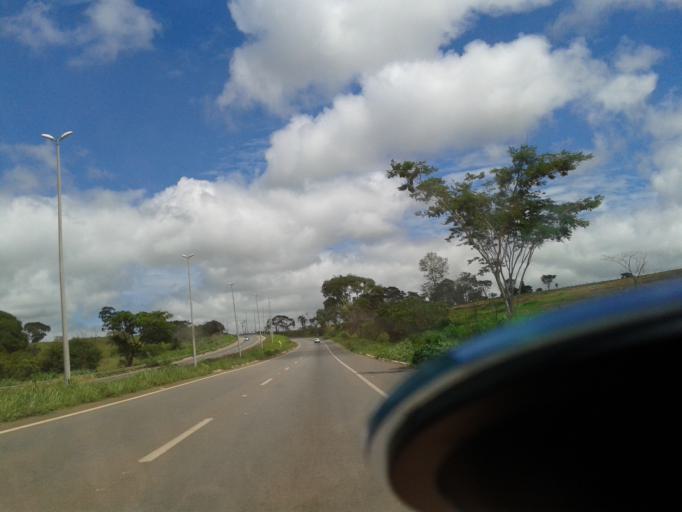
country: BR
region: Goias
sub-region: Inhumas
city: Inhumas
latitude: -16.4098
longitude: -49.4760
